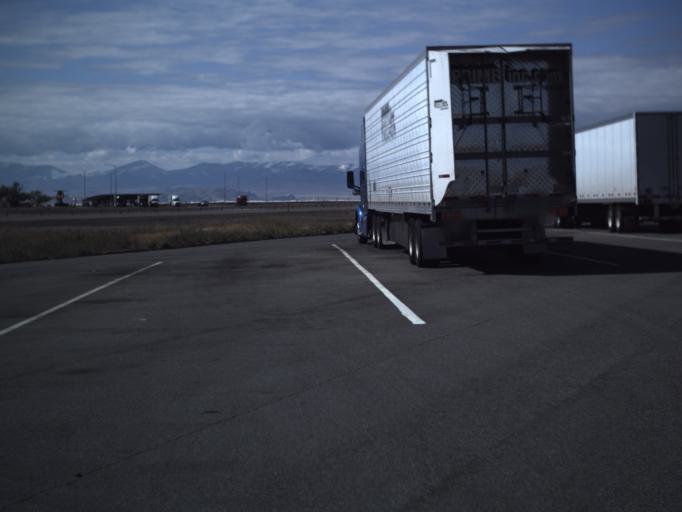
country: US
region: Utah
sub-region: Tooele County
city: Wendover
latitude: 40.7401
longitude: -113.8518
